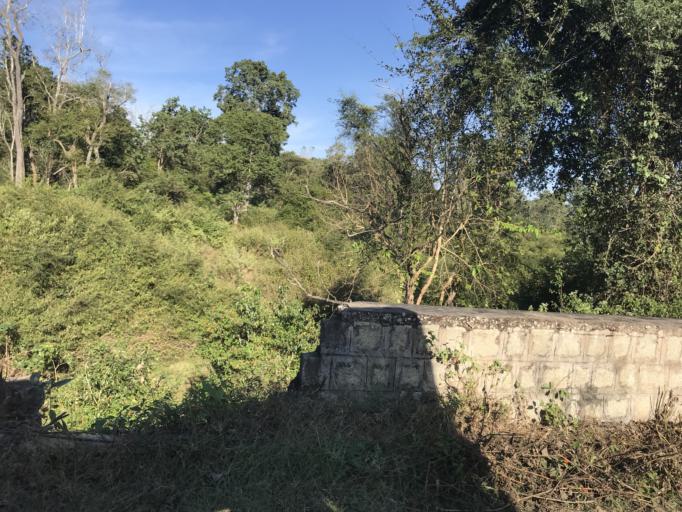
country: IN
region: Karnataka
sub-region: Mysore
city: Heggadadevankote
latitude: 11.9762
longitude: 76.2403
